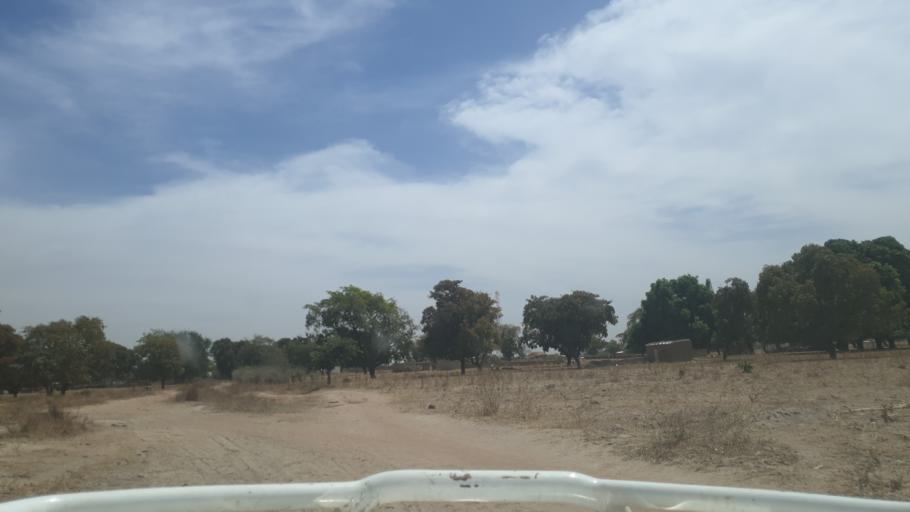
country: ML
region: Sikasso
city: Yorosso
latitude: 12.2915
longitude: -4.6593
